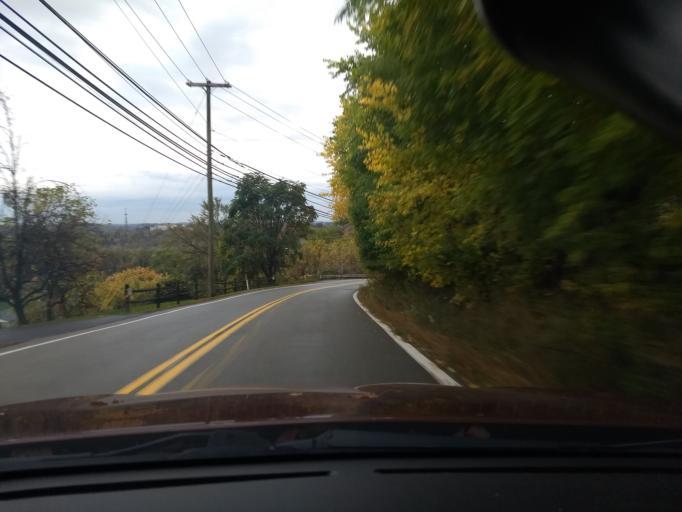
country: US
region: Pennsylvania
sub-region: Allegheny County
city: Jefferson Hills
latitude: 40.3056
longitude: -79.9424
